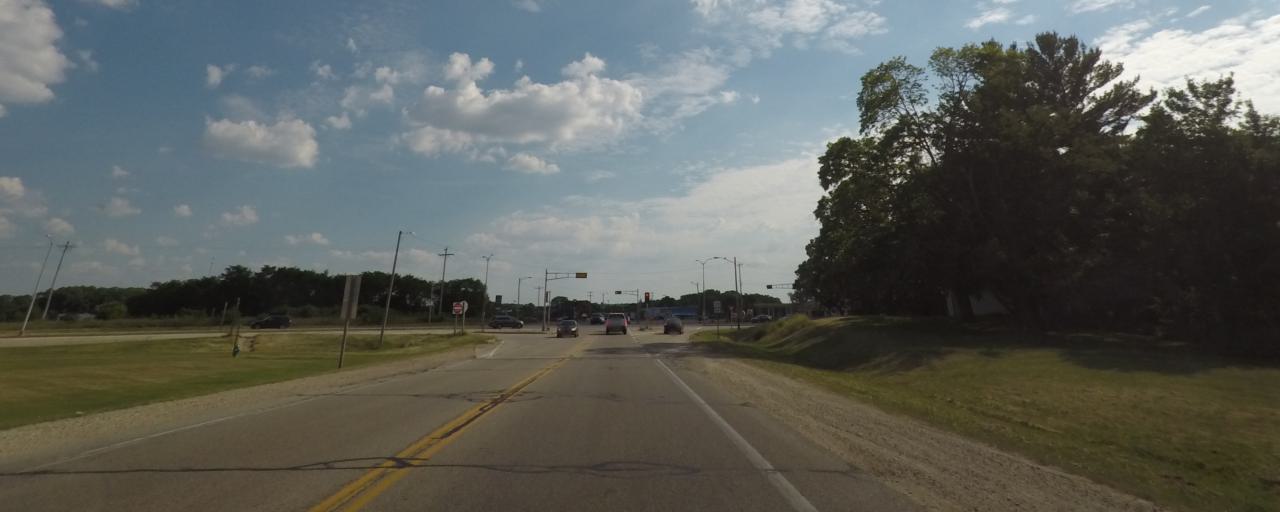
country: US
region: Wisconsin
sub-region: Walworth County
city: East Troy
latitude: 42.7931
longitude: -88.3887
